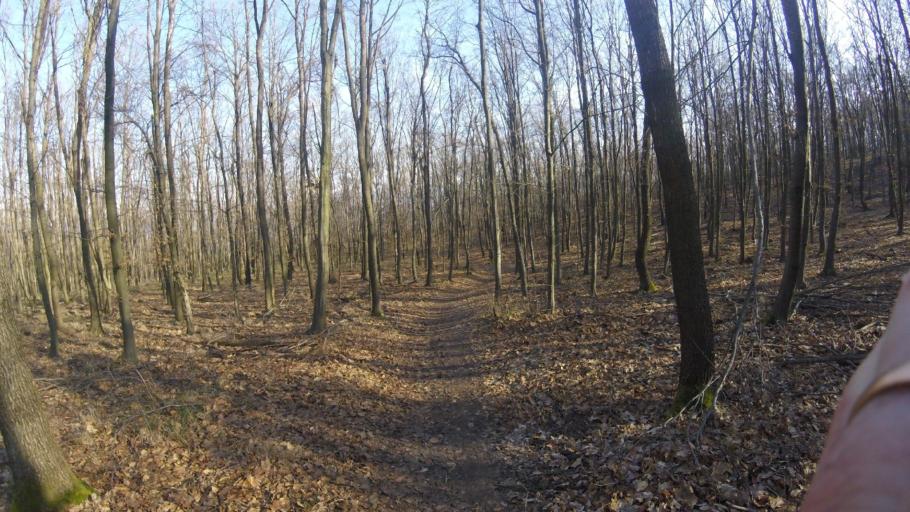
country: HU
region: Pest
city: Pilisszentkereszt
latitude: 47.6627
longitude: 18.9245
